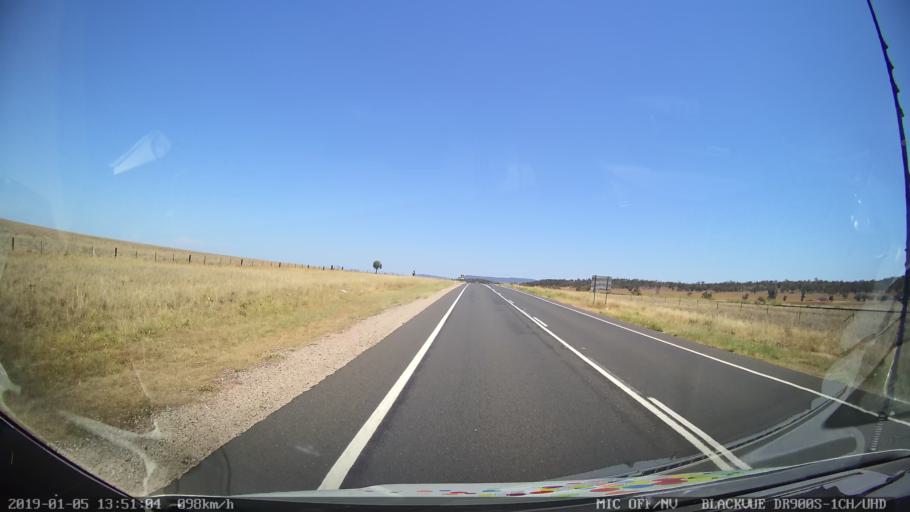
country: AU
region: New South Wales
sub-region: Gunnedah
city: Gunnedah
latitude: -31.0392
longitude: 150.2762
